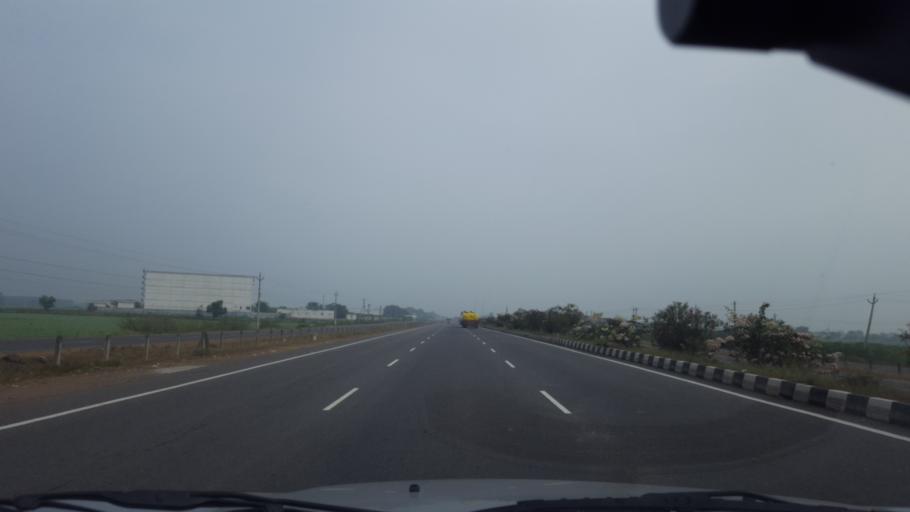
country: IN
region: Andhra Pradesh
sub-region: Guntur
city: Chilakalurupet
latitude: 16.0366
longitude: 80.1336
